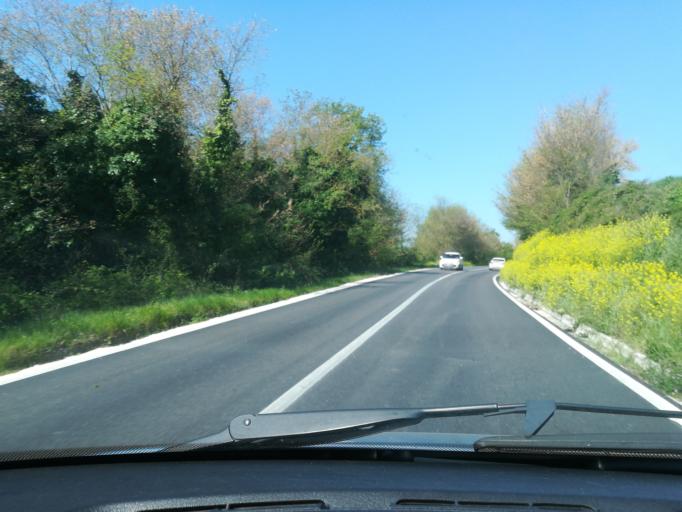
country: IT
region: The Marches
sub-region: Provincia di Macerata
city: Villa Potenza
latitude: 43.3287
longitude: 13.3914
